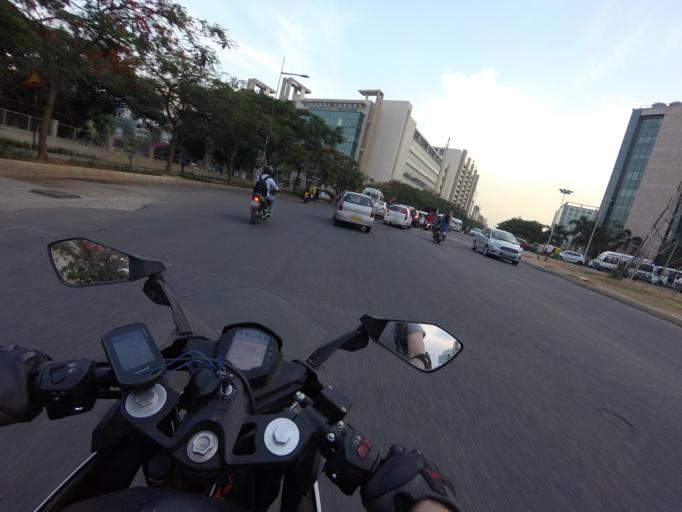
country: IN
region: Karnataka
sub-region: Bangalore Urban
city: Yelahanka
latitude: 13.0492
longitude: 77.6194
